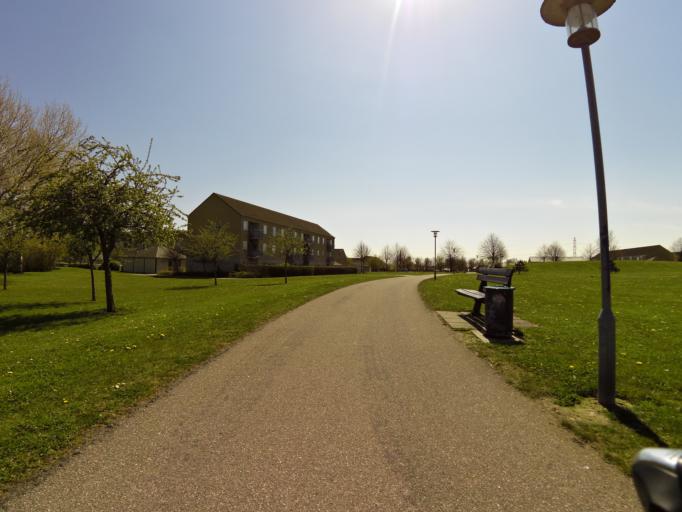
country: DK
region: Capital Region
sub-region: Hoje-Taastrup Kommune
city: Taastrup
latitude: 55.6372
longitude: 12.2730
